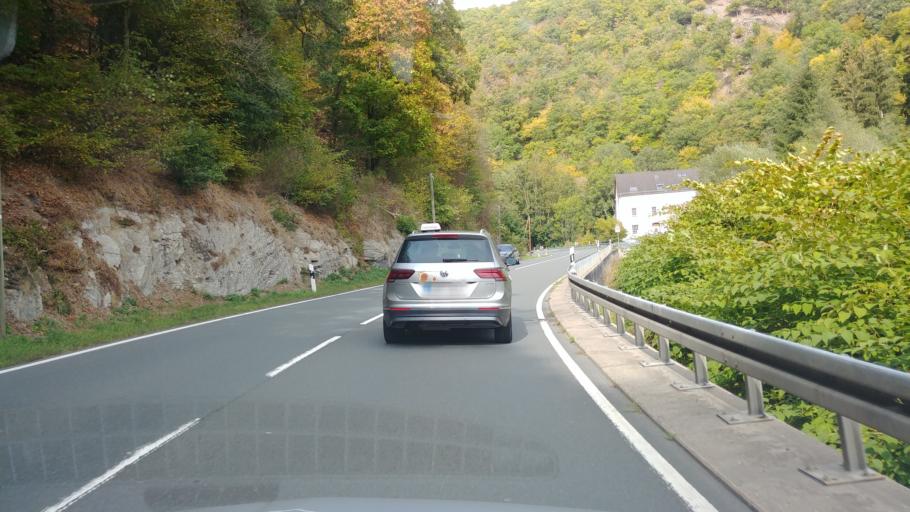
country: DE
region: Hesse
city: Burg Hohenstein
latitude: 50.1964
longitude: 8.0574
